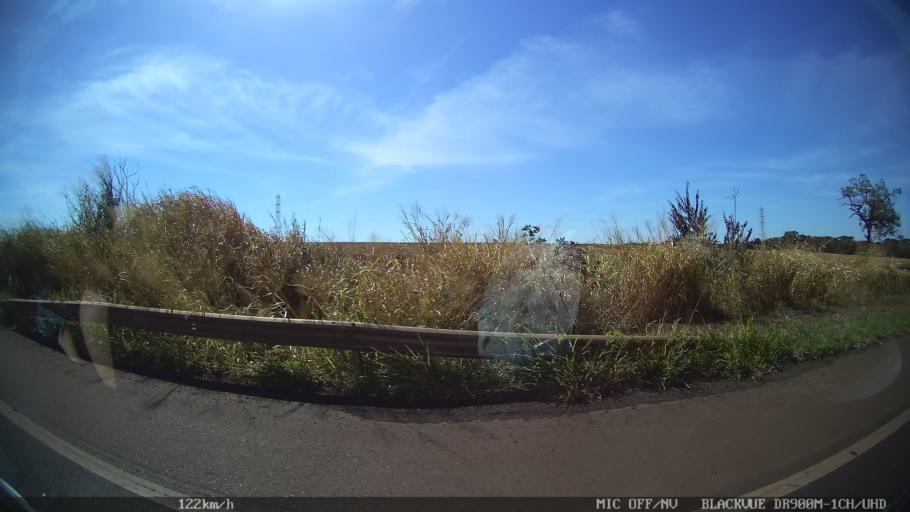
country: BR
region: Sao Paulo
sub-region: Ipua
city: Ipua
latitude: -20.4590
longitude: -48.1485
